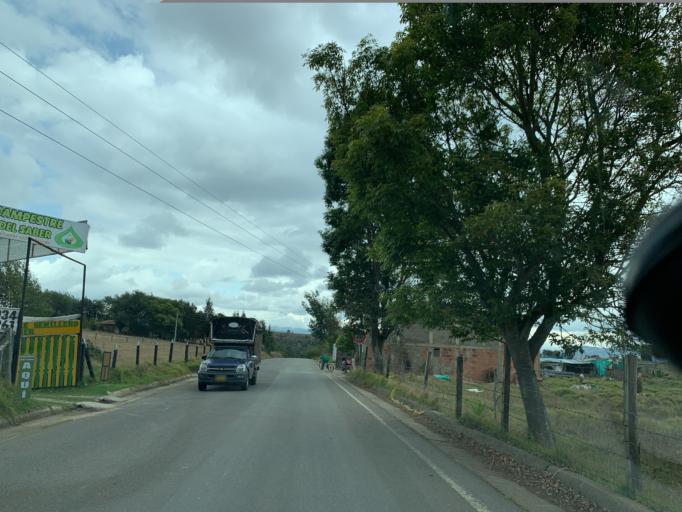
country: CO
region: Boyaca
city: Tunja
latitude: 5.5710
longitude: -73.3651
